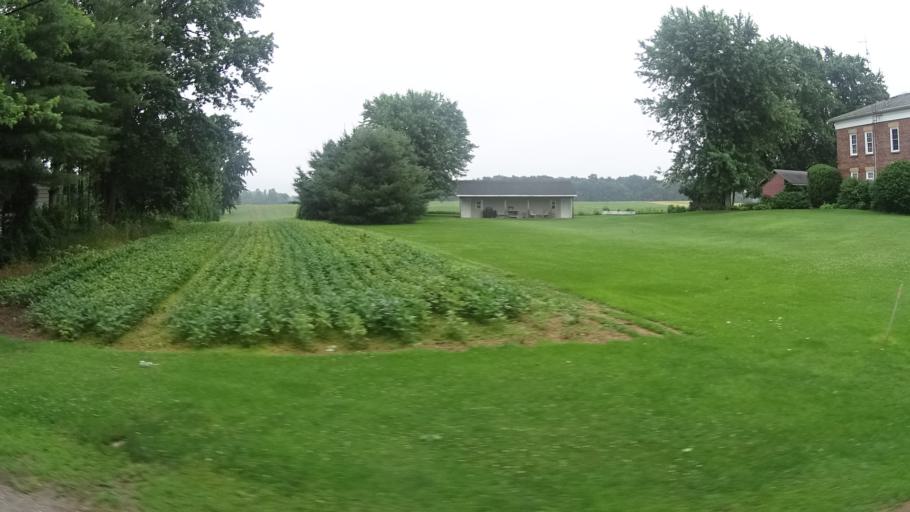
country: US
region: Ohio
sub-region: Erie County
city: Milan
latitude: 41.3565
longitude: -82.6024
